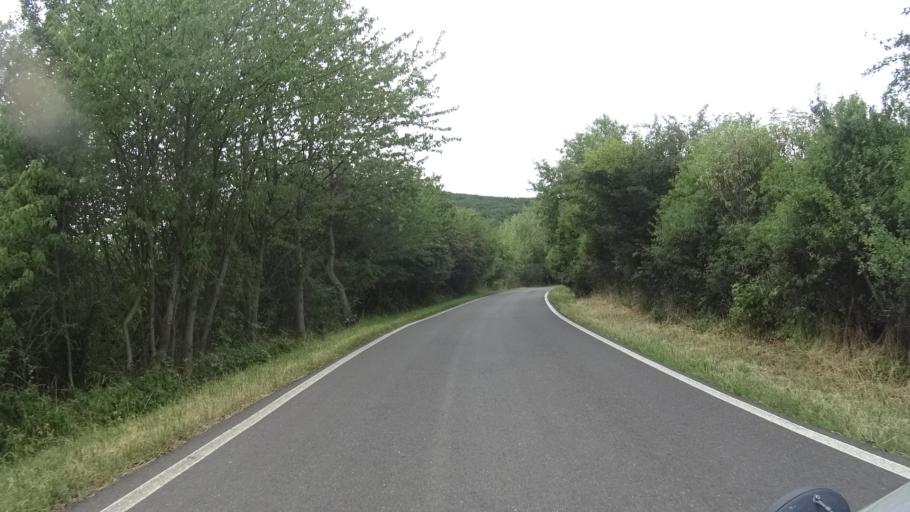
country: CZ
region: Ustecky
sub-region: Okres Litomerice
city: Litomerice
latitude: 50.5651
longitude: 14.1214
